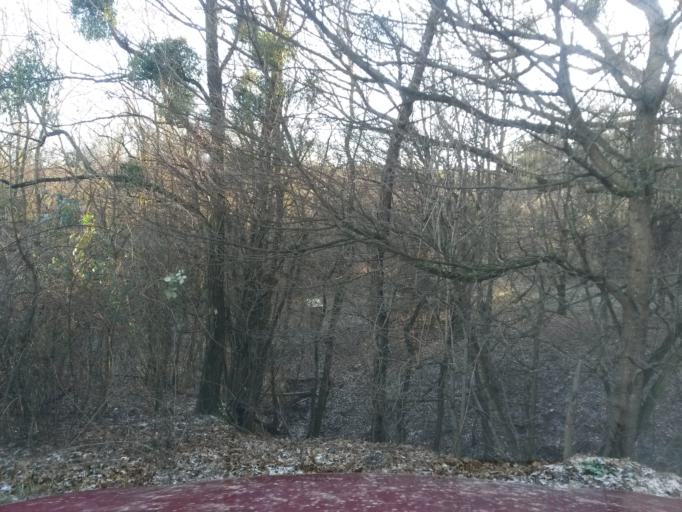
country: HU
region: Borsod-Abauj-Zemplen
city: Sarospatak
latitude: 48.3311
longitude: 21.5108
